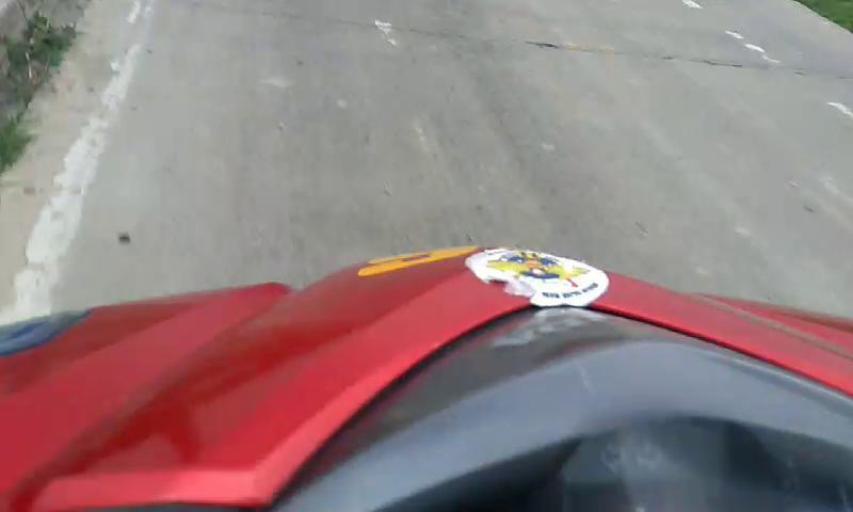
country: ID
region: West Java
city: Bekasi
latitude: -6.1455
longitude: 106.9702
